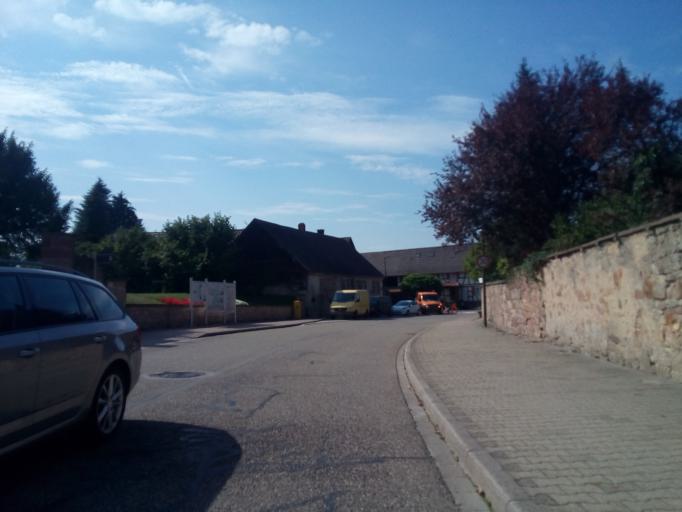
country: DE
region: Baden-Wuerttemberg
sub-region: Karlsruhe Region
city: Ottersweier
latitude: 48.6676
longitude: 8.1123
